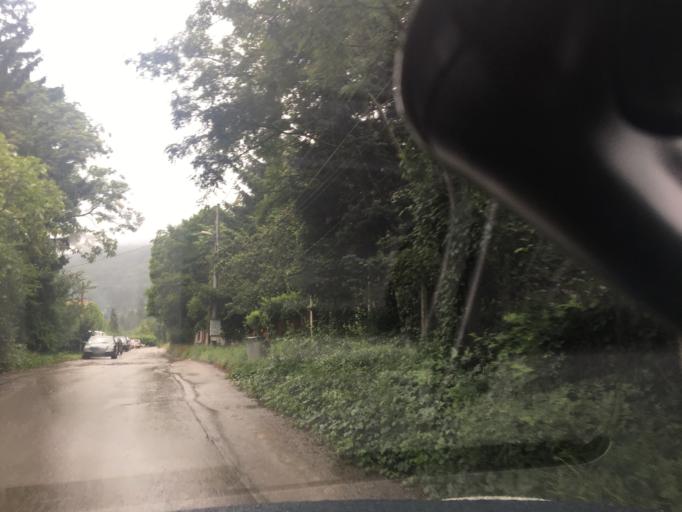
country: BG
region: Sofia-Capital
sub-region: Stolichna Obshtina
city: Sofia
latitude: 42.5849
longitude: 23.3478
